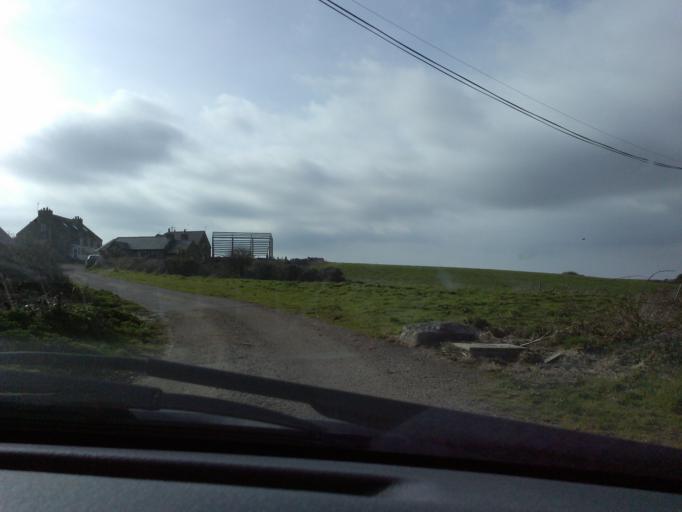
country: GB
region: England
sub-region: Cornwall
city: St. Buryan
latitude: 50.0441
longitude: -5.6549
